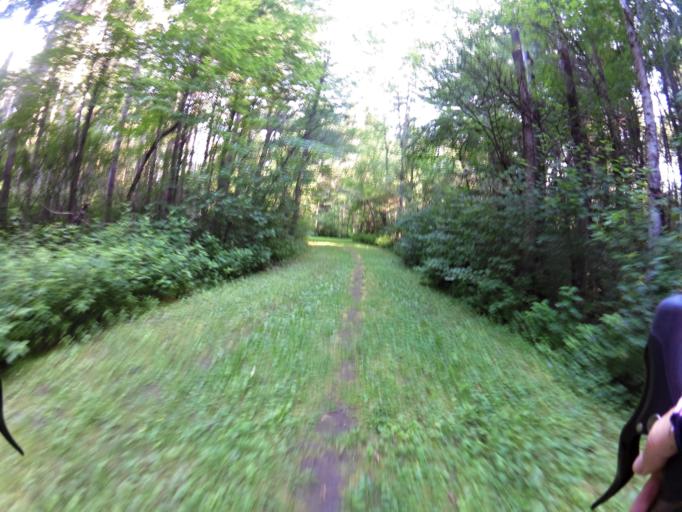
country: CA
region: Ontario
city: Bells Corners
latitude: 45.3145
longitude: -75.7340
